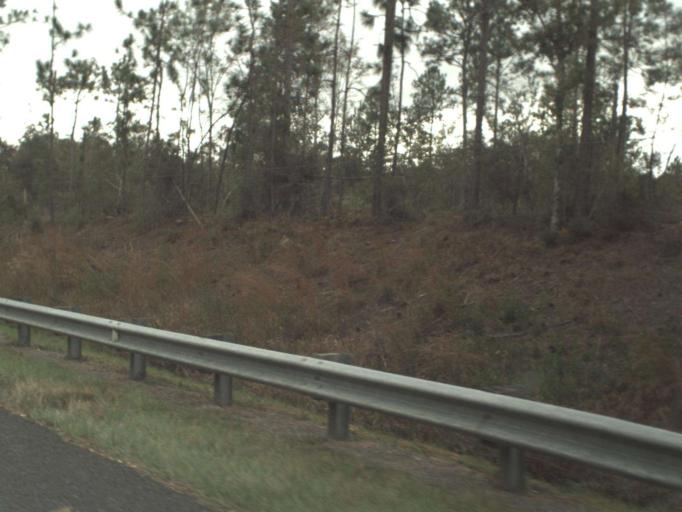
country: US
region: Florida
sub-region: Escambia County
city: Molino
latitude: 30.8276
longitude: -87.3331
